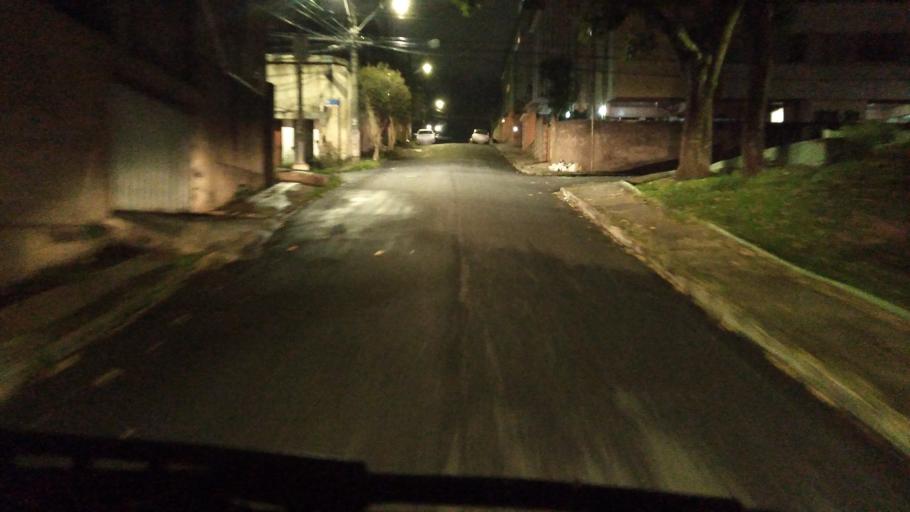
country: BR
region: Minas Gerais
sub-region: Belo Horizonte
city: Belo Horizonte
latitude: -19.9000
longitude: -43.9190
